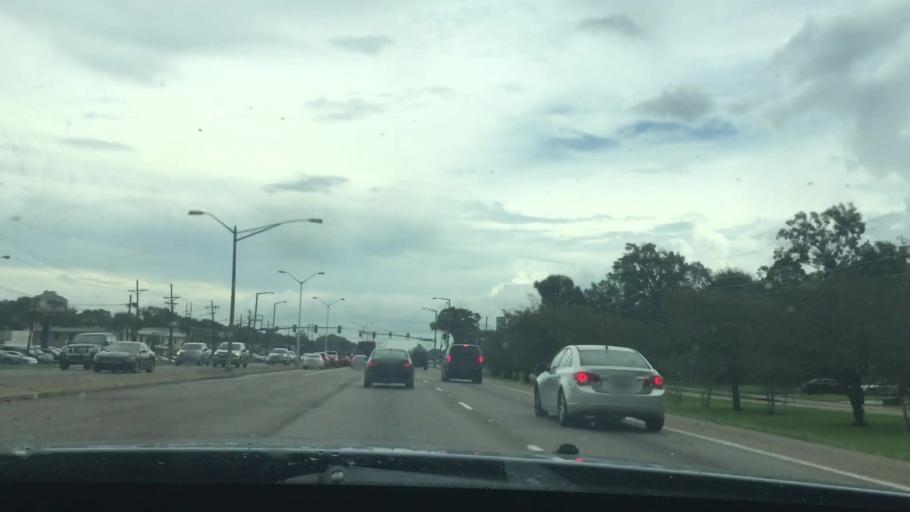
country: US
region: Louisiana
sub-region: East Baton Rouge Parish
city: Westminster
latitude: 30.4529
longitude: -91.0925
